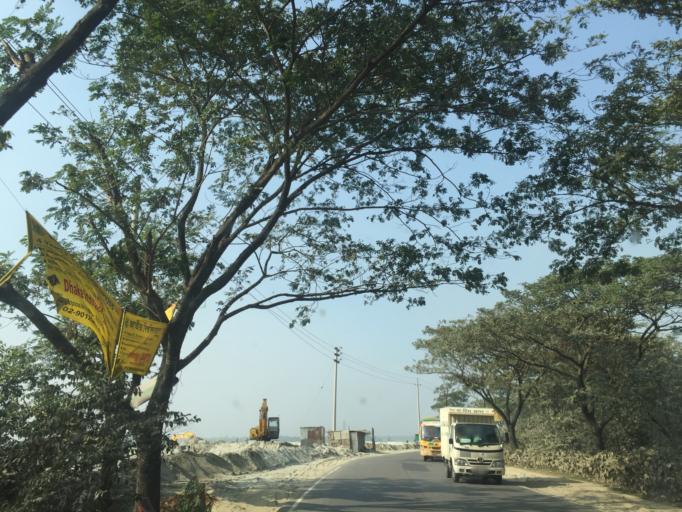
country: BD
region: Dhaka
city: Tungi
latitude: 23.8309
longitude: 90.3412
